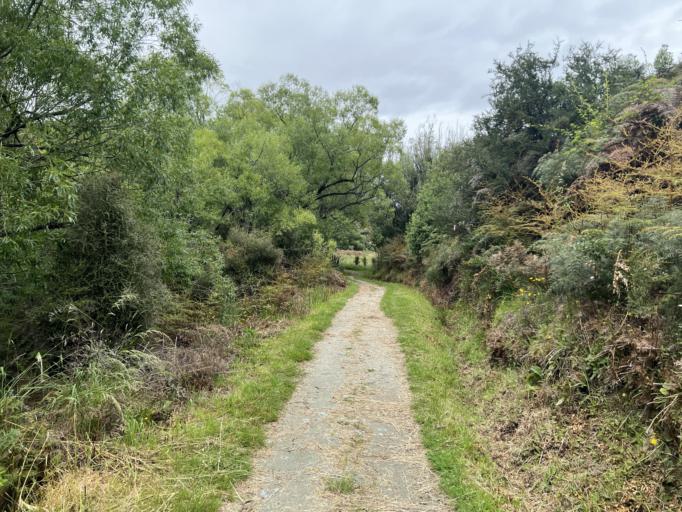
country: NZ
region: Otago
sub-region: Queenstown-Lakes District
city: Wanaka
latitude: -44.6479
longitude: 168.9624
